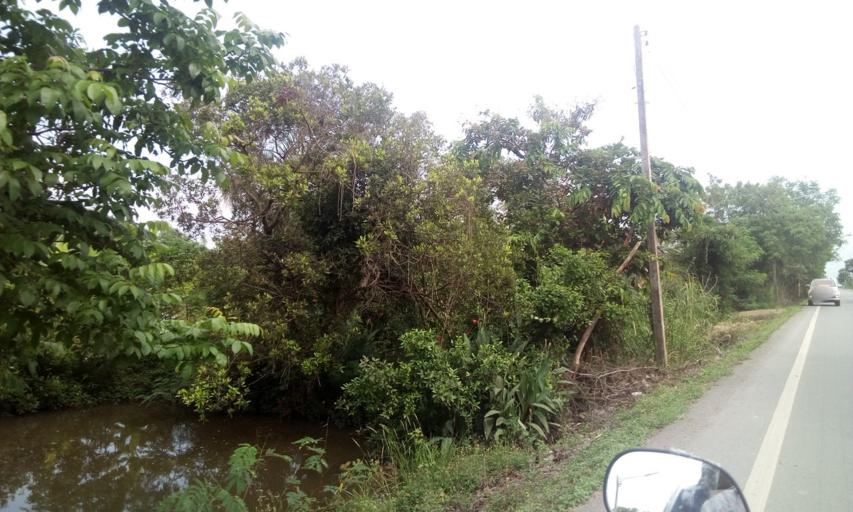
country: TH
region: Pathum Thani
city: Ban Lam Luk Ka
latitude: 13.9948
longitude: 100.8420
